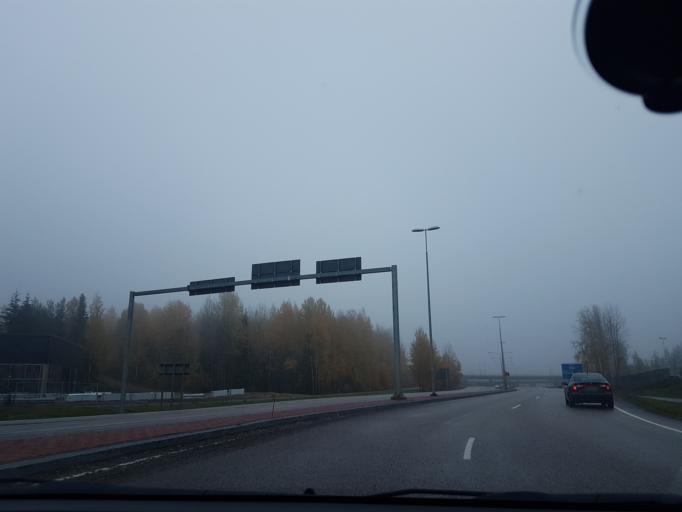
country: FI
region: Uusimaa
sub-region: Helsinki
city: Jaervenpaeae
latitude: 60.4557
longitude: 25.1178
